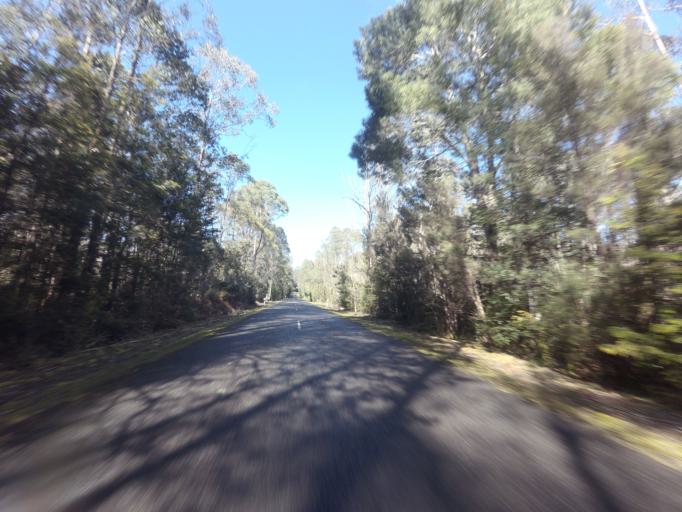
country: AU
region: Tasmania
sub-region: Derwent Valley
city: New Norfolk
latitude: -42.7341
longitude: 146.4250
